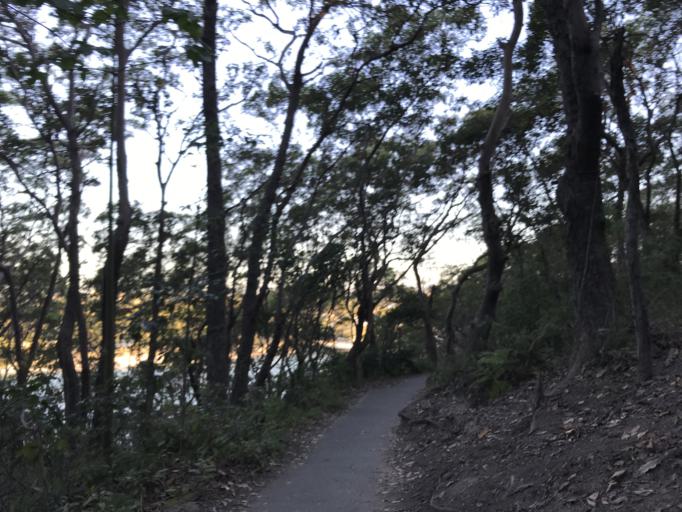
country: AU
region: Queensland
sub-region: Gold Coast
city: Palm Beach
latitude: -28.0961
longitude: 153.4569
